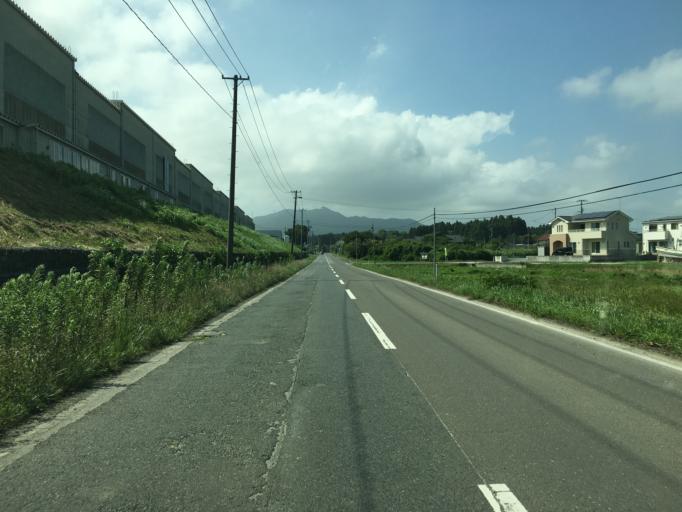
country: JP
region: Miyagi
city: Marumori
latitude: 37.8354
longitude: 140.9067
